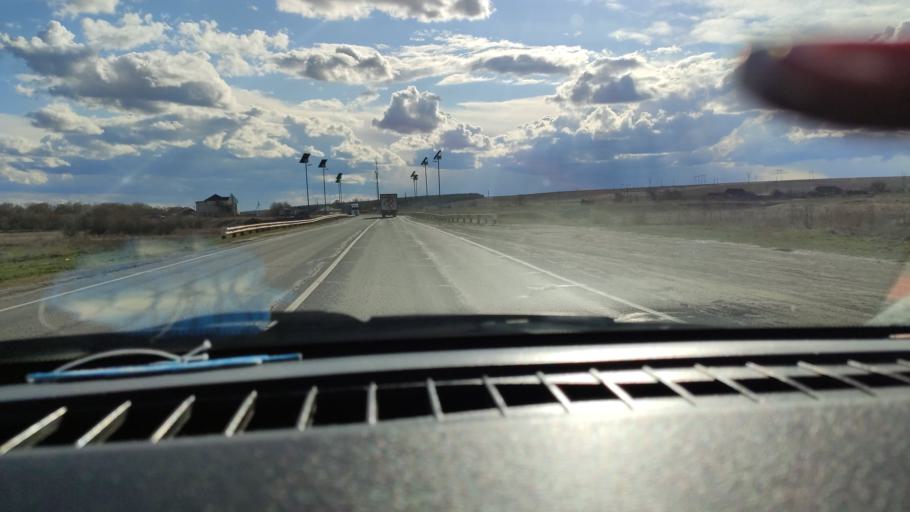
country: RU
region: Saratov
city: Sinodskoye
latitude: 52.0480
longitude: 46.7456
